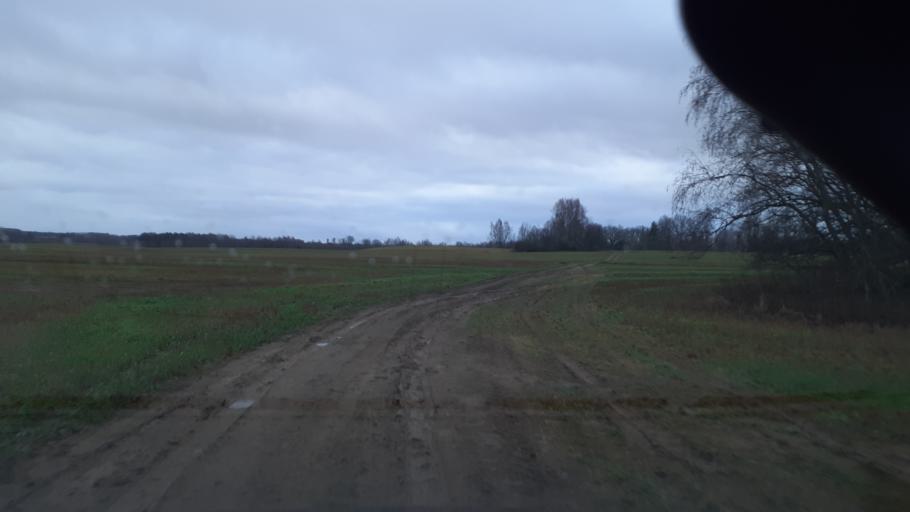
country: LV
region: Kuldigas Rajons
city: Kuldiga
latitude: 56.8838
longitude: 21.7703
